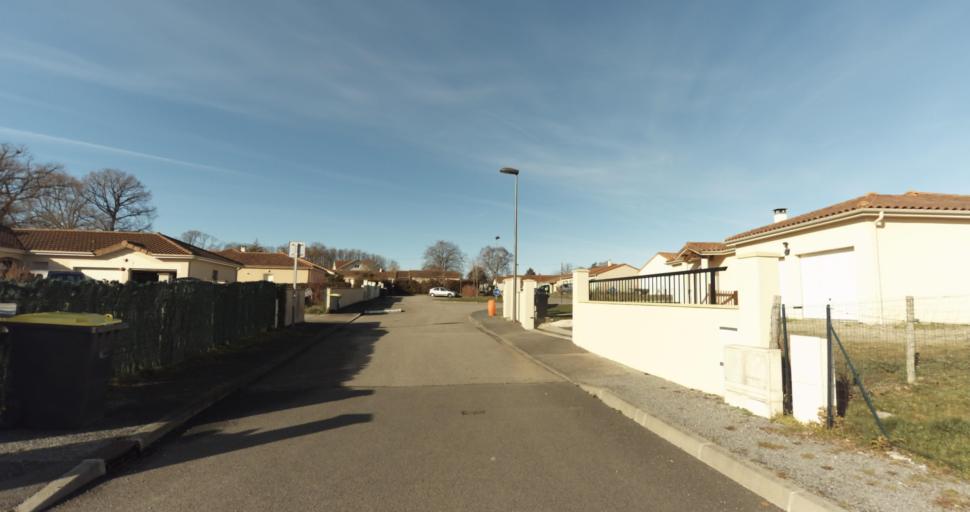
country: FR
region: Limousin
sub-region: Departement de la Haute-Vienne
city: Aixe-sur-Vienne
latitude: 45.7898
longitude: 1.1244
